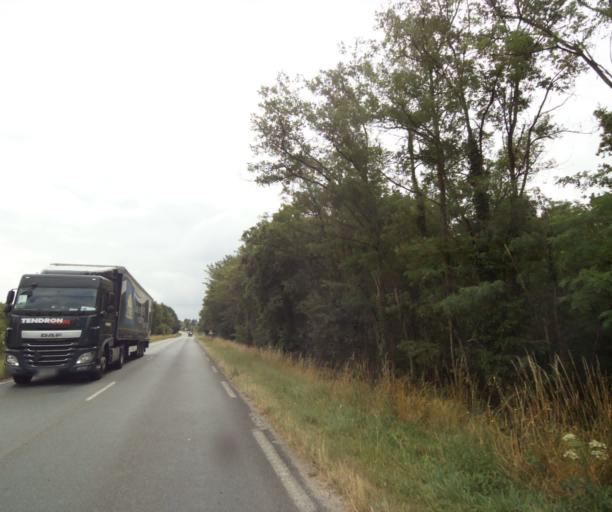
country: FR
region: Centre
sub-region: Departement du Loiret
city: Darvoy
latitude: 47.8772
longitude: 2.1068
